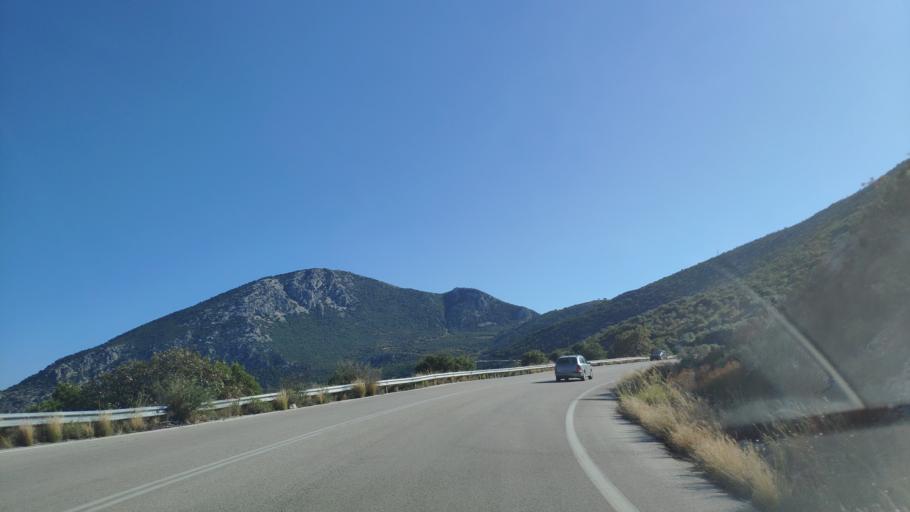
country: GR
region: Peloponnese
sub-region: Nomos Argolidos
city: Palaia Epidavros
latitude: 37.6131
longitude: 23.1516
